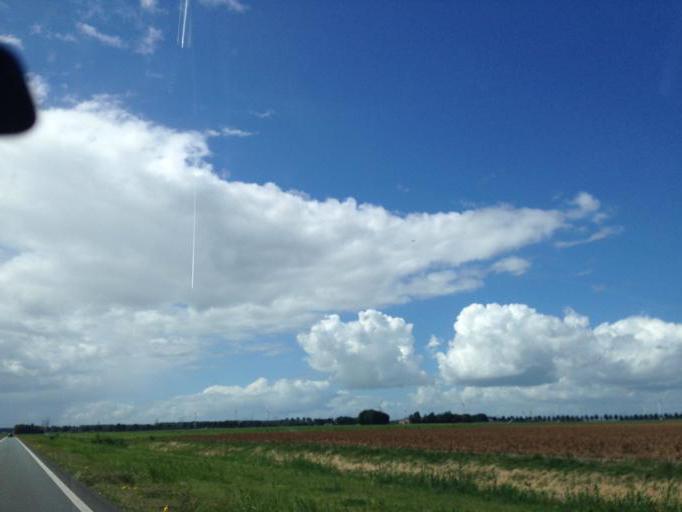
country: NL
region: Flevoland
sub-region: Gemeente Urk
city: Urk
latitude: 52.5490
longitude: 5.5828
